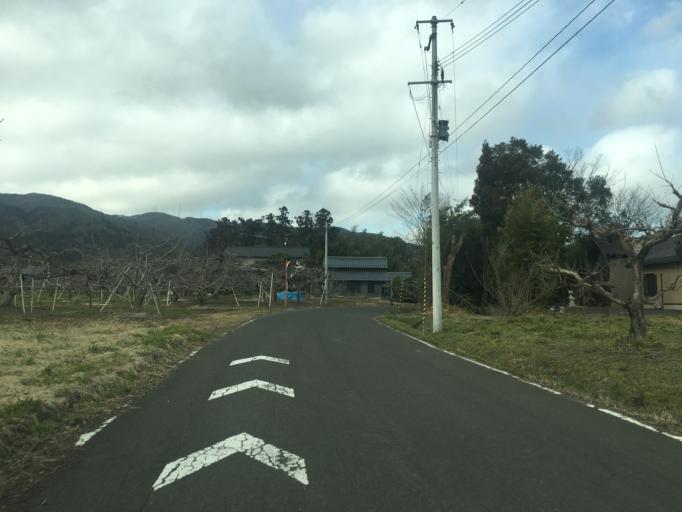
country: JP
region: Fukushima
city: Yanagawamachi-saiwaicho
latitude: 37.8868
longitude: 140.5818
